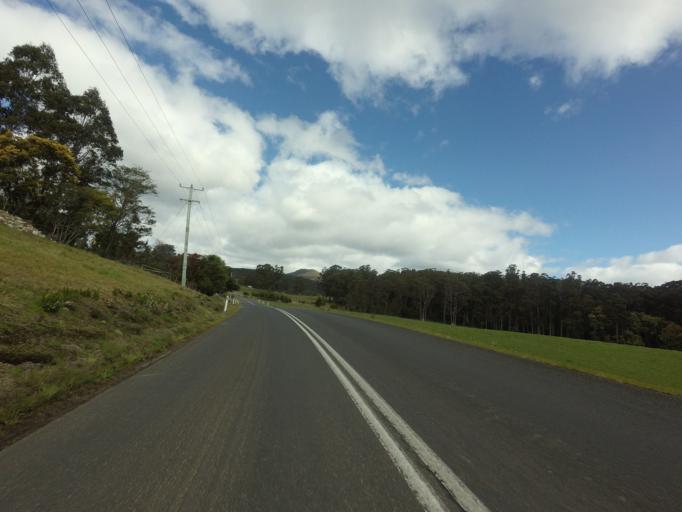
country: AU
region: Tasmania
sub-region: Huon Valley
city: Geeveston
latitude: -43.1933
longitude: 146.9388
